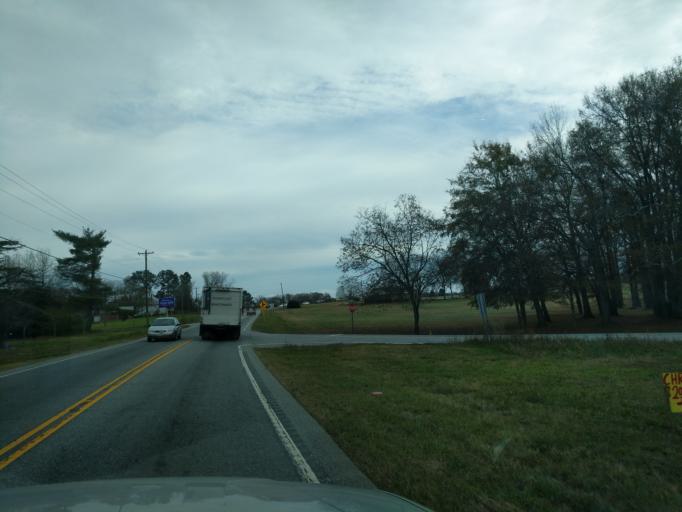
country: US
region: South Carolina
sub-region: Anderson County
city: Williamston
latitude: 34.6507
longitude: -82.4876
